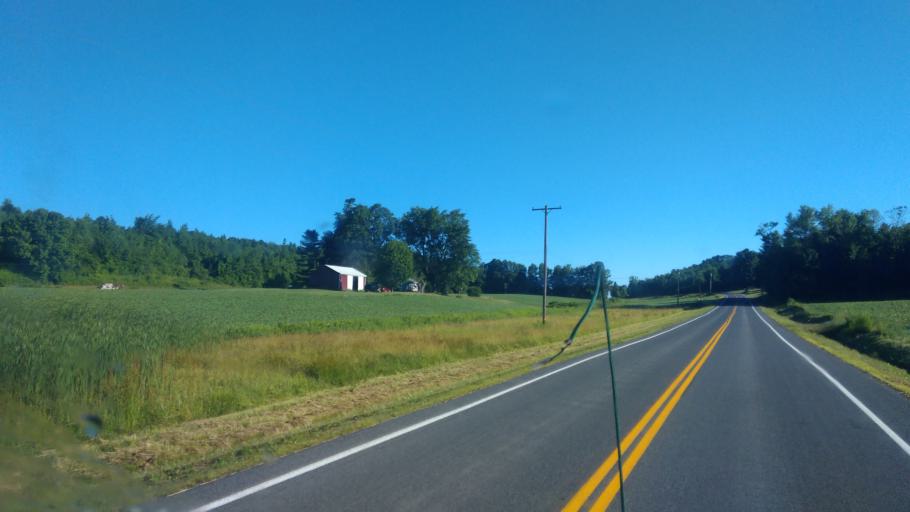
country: US
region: New York
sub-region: Wayne County
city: Sodus
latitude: 43.1511
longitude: -77.0483
